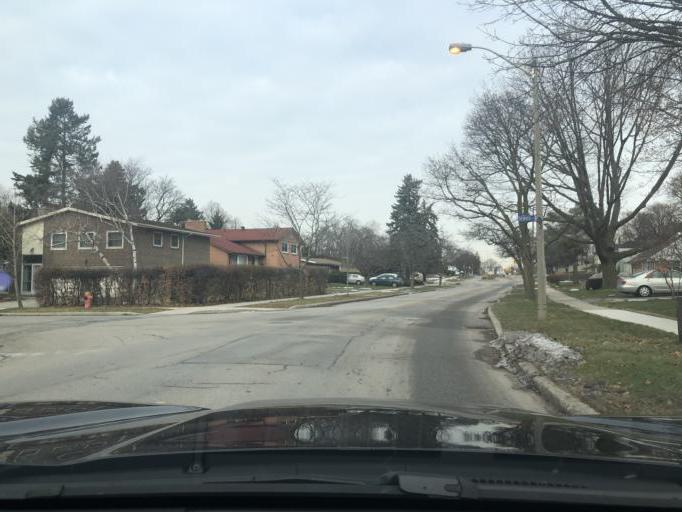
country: CA
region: Ontario
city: Willowdale
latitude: 43.7721
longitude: -79.3526
